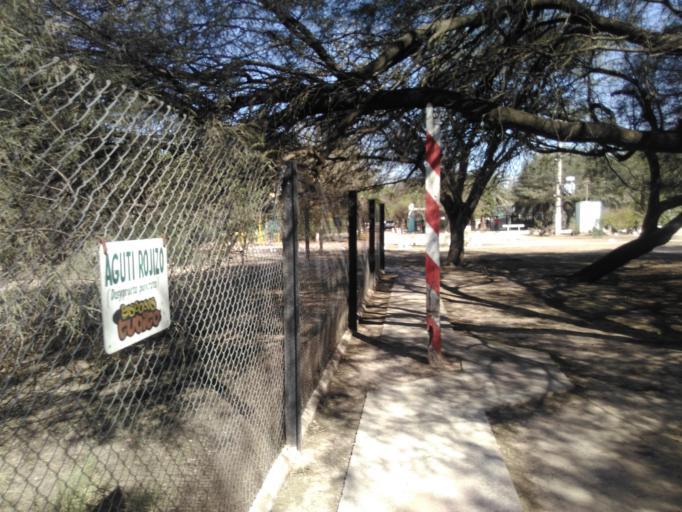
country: AR
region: Chaco
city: Presidencia Roque Saenz Pena
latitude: -26.8164
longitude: -60.4181
